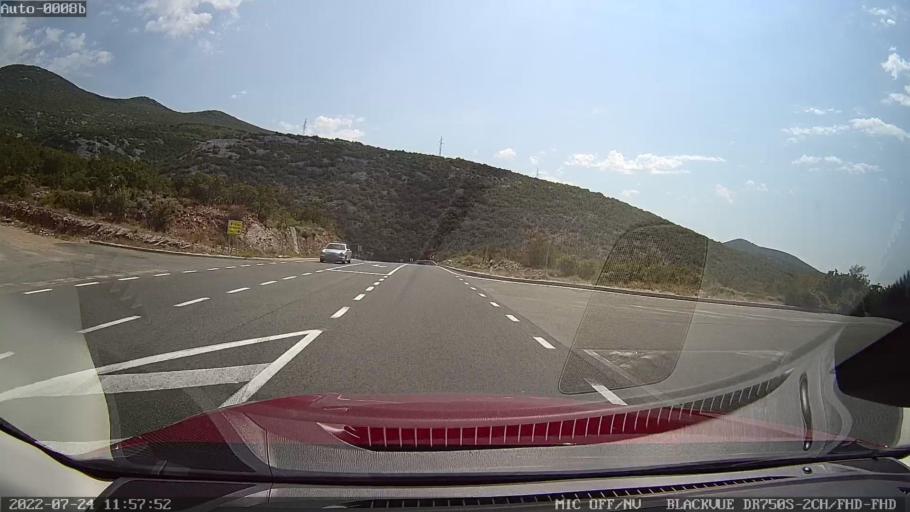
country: HR
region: Primorsko-Goranska
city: Novi Vinodolski
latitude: 45.1185
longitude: 14.8441
